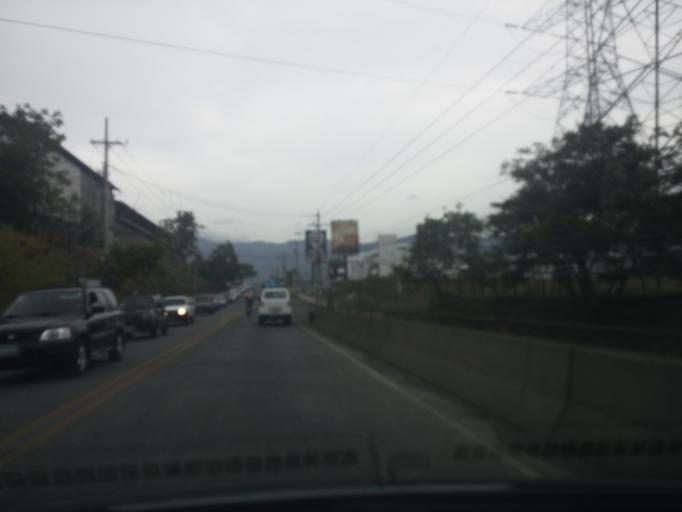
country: CR
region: Heredia
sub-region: Canton de Belen
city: San Antonio
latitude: 9.9651
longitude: -84.1988
